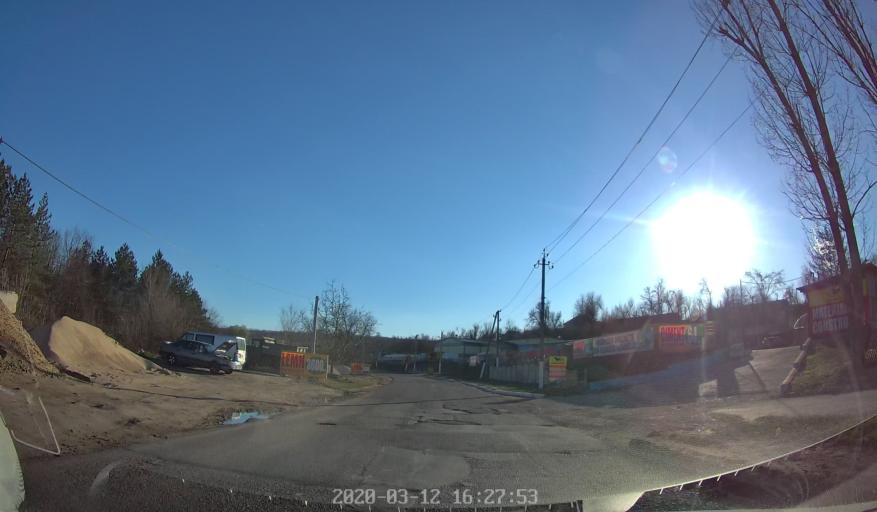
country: MD
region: Anenii Noi
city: Anenii Noi
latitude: 46.8725
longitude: 29.2272
